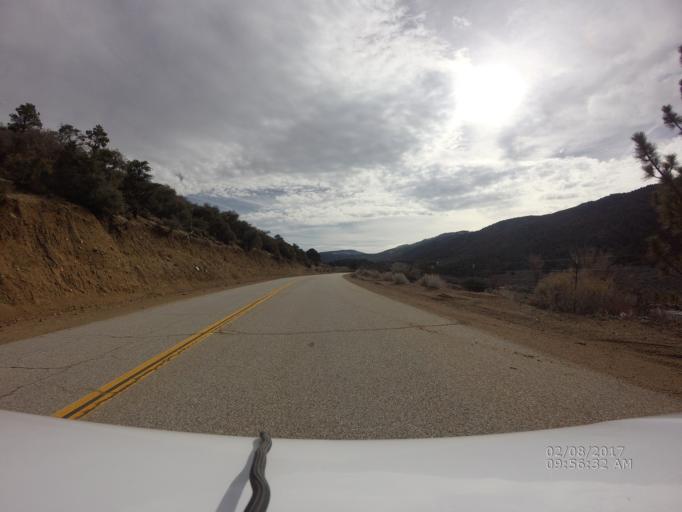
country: US
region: California
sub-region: San Bernardino County
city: Pinon Hills
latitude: 34.4160
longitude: -117.7810
